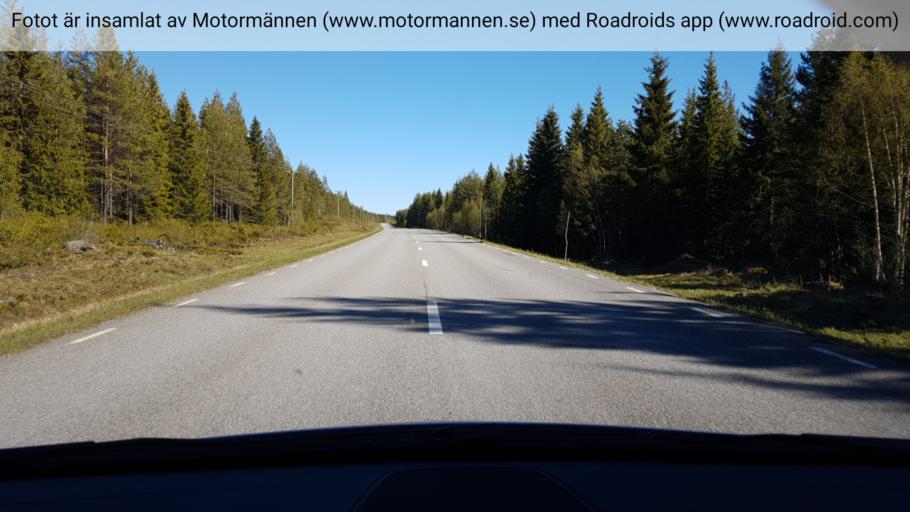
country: SE
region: Jaemtland
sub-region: Stroemsunds Kommun
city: Stroemsund
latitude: 64.2828
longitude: 15.3574
